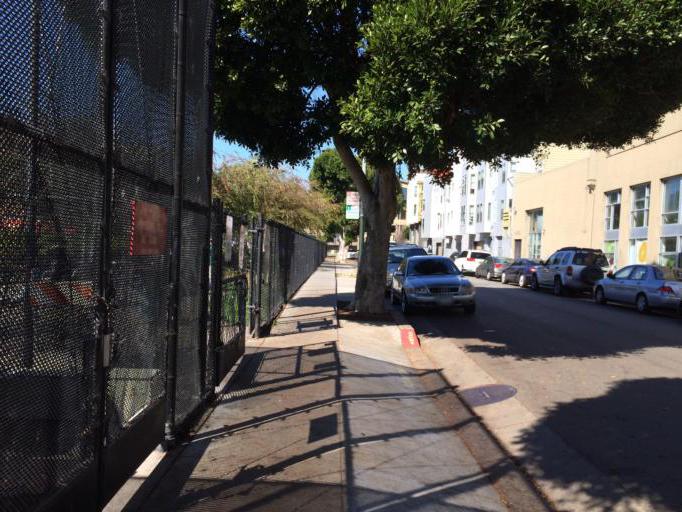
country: US
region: California
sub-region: San Francisco County
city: San Francisco
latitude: 37.7771
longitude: -122.4055
